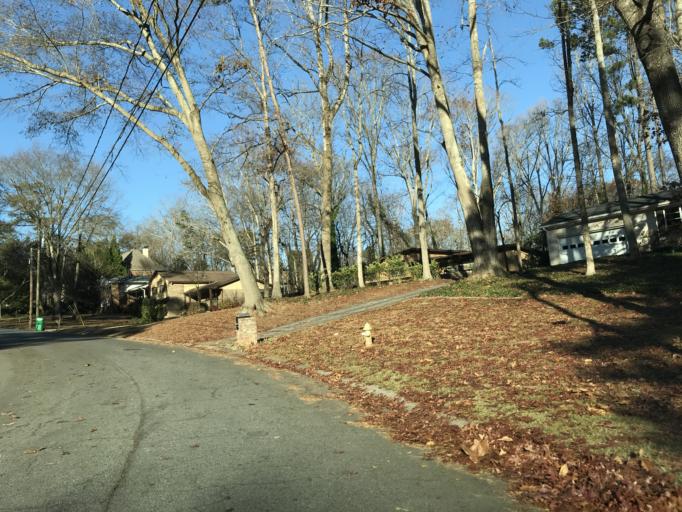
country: US
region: Georgia
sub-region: DeKalb County
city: North Atlanta
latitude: 33.8882
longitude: -84.3391
